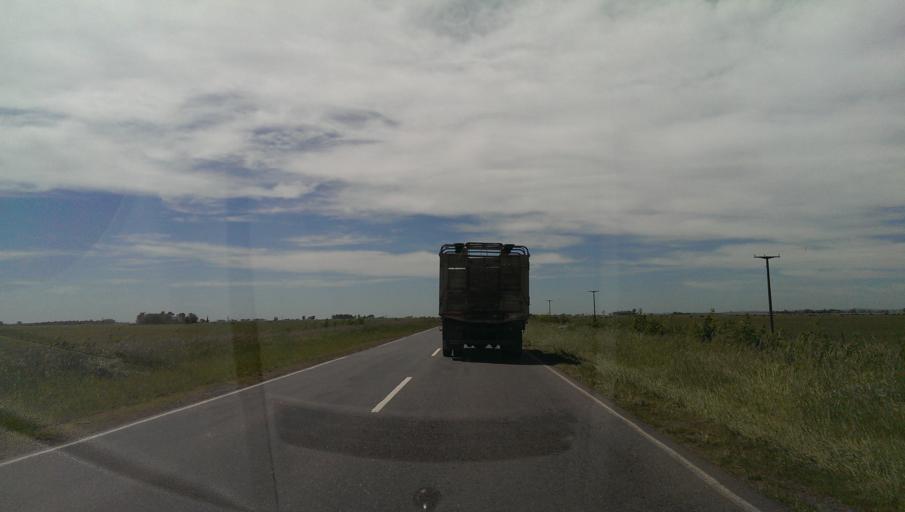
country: AR
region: Buenos Aires
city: Olavarria
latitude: -37.0672
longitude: -60.4668
